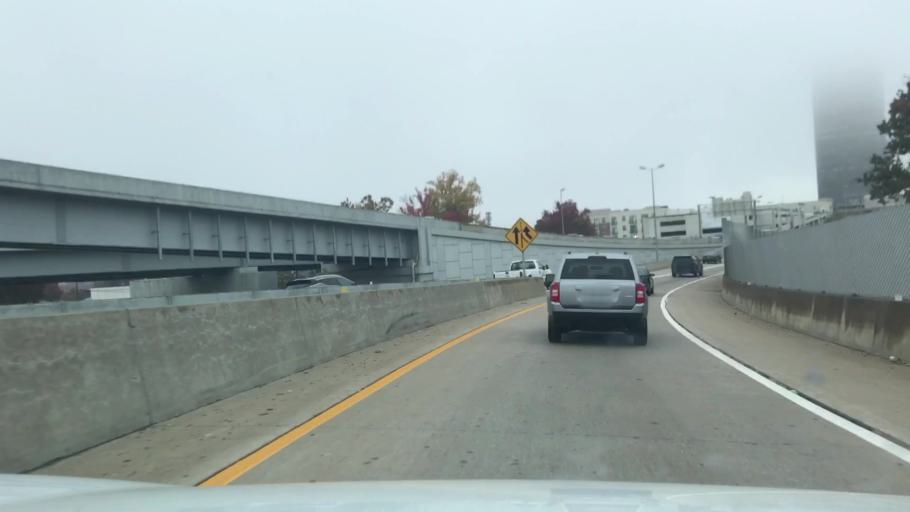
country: US
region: Missouri
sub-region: Saint Louis County
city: Brentwood
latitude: 38.6314
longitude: -90.3440
